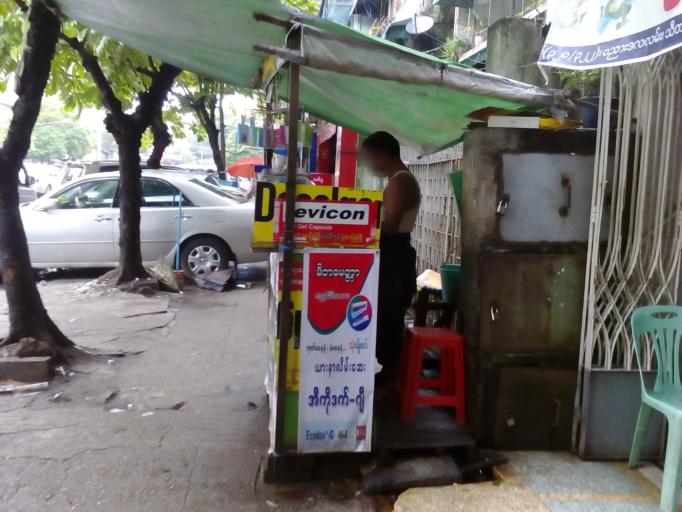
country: MM
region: Yangon
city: Yangon
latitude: 16.7995
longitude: 96.1759
